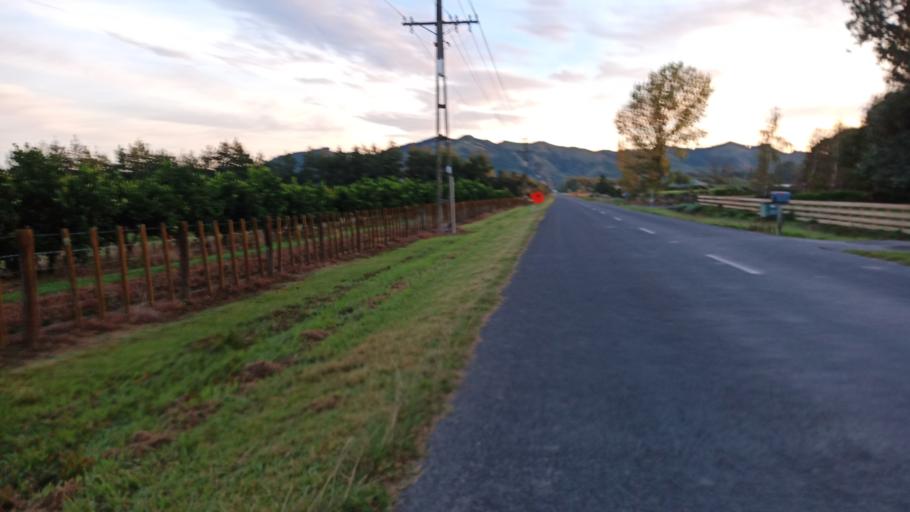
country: NZ
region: Gisborne
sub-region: Gisborne District
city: Gisborne
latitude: -38.6303
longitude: 177.9750
